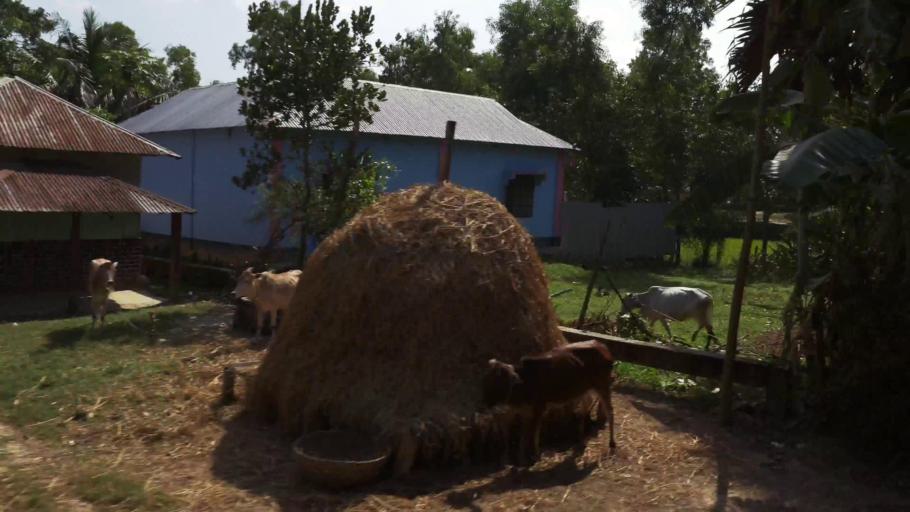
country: BD
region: Dhaka
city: Gafargaon
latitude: 24.2218
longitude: 90.4865
